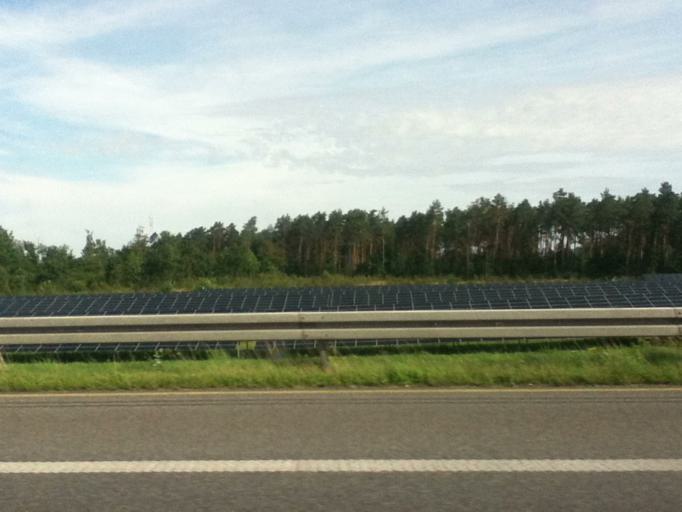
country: DE
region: Saxony
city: Ottendorf-Okrilla
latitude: 51.1719
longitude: 13.8487
